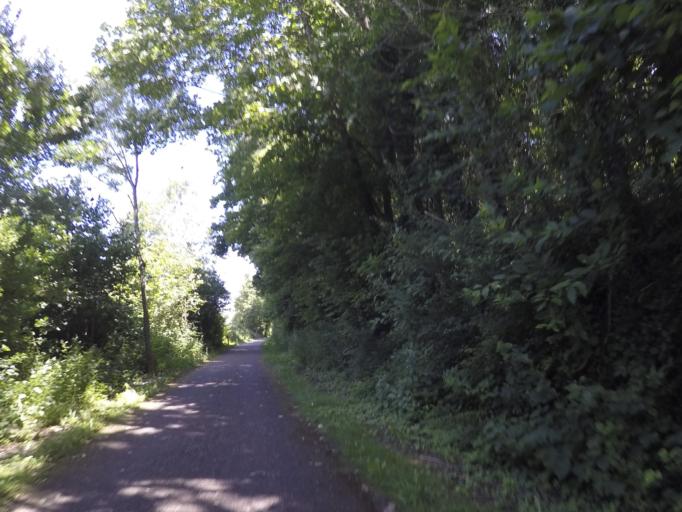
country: BE
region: Wallonia
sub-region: Province de Namur
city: Ciney
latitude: 50.3184
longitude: 5.1082
